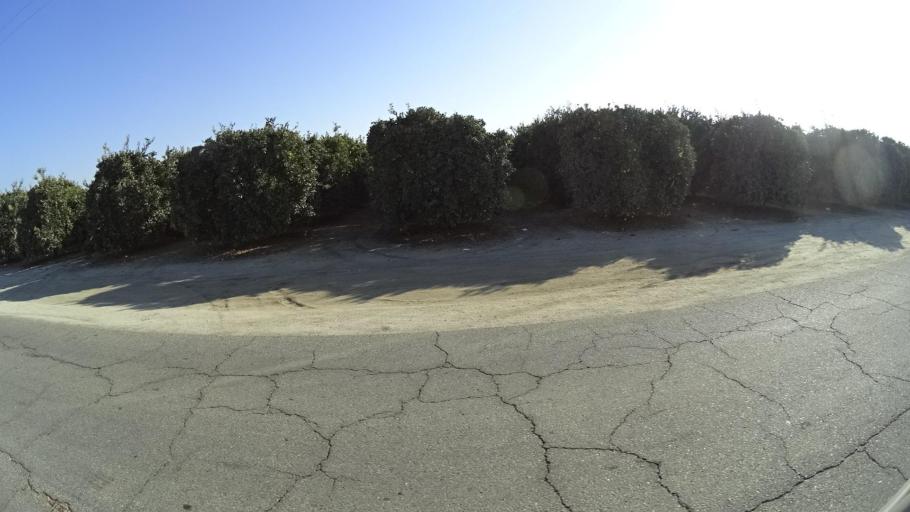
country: US
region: California
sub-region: Tulare County
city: Richgrove
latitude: 35.7895
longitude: -119.1698
